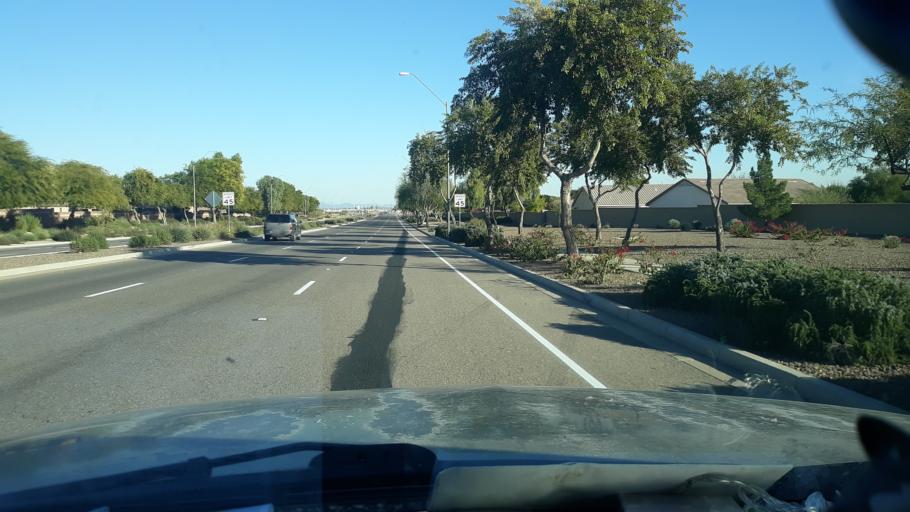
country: US
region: Arizona
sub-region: Maricopa County
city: Citrus Park
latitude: 33.5661
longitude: -112.4524
